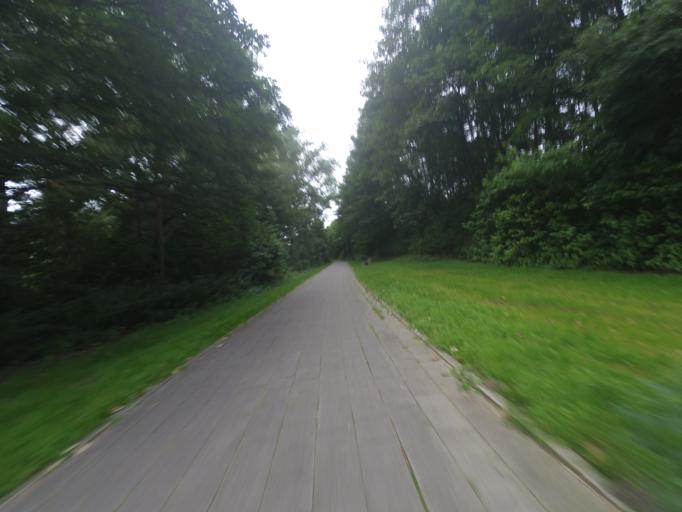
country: DE
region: Hamburg
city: Wandsbek
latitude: 53.5337
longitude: 10.1121
